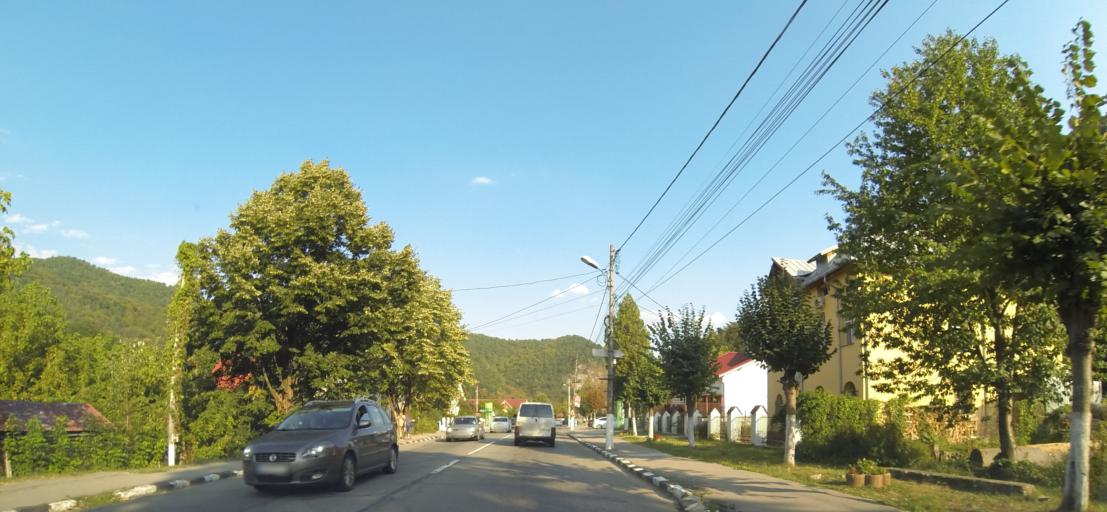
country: RO
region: Valcea
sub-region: Oras Calimanesti
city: Calimanesti
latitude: 45.2589
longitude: 24.3268
